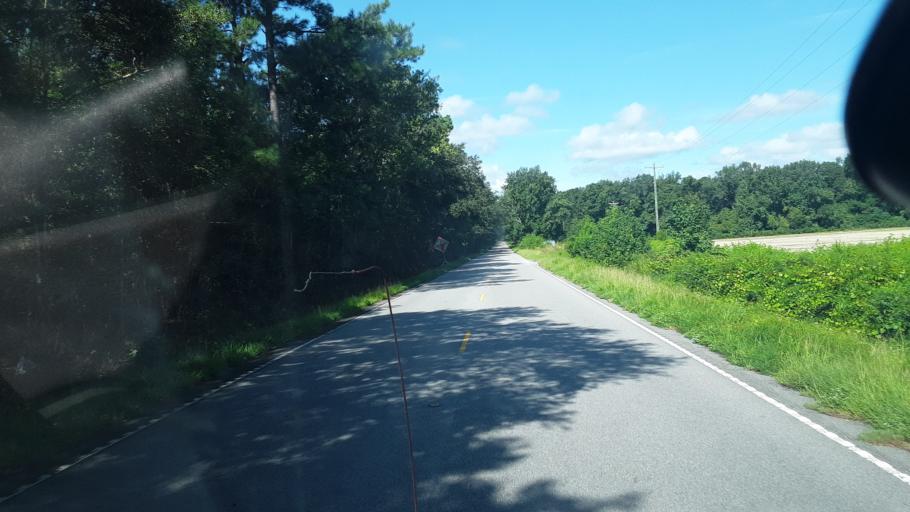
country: US
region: South Carolina
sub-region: Jasper County
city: Ridgeland
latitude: 32.5896
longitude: -80.9522
